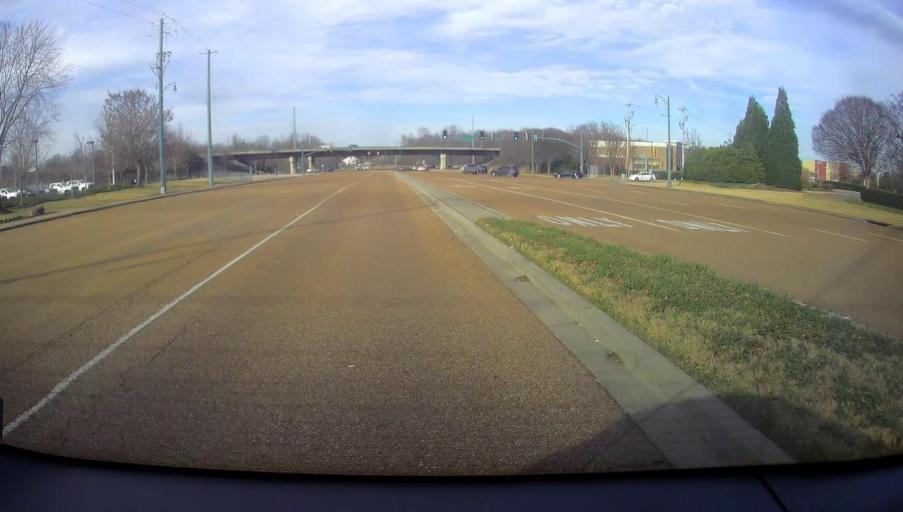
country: US
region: Tennessee
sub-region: Shelby County
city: Collierville
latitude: 35.0234
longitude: -89.7228
